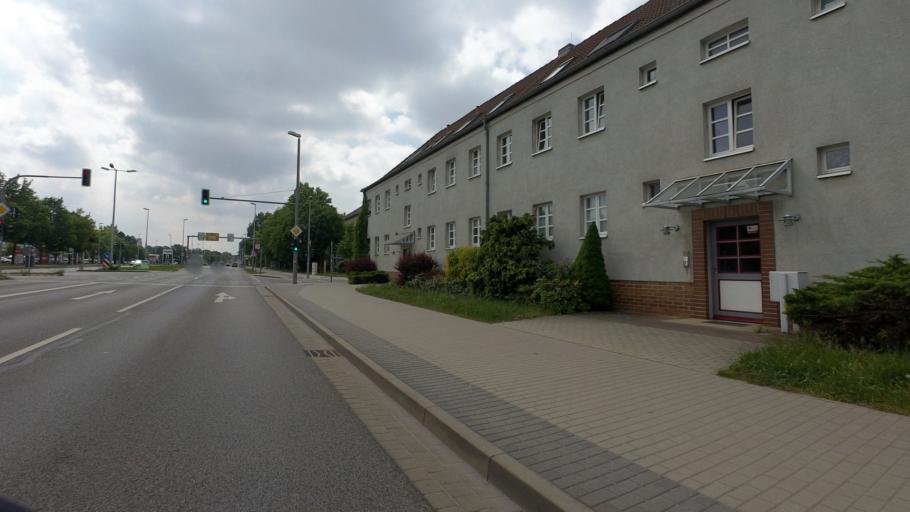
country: DE
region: Brandenburg
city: Cottbus
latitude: 51.7650
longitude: 14.3584
